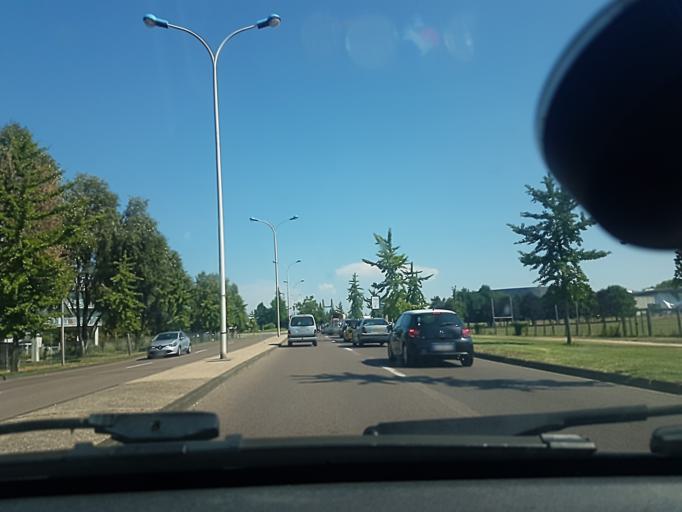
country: FR
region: Bourgogne
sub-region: Departement de Saone-et-Loire
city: Chalon-sur-Saone
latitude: 46.7895
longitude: 4.8636
